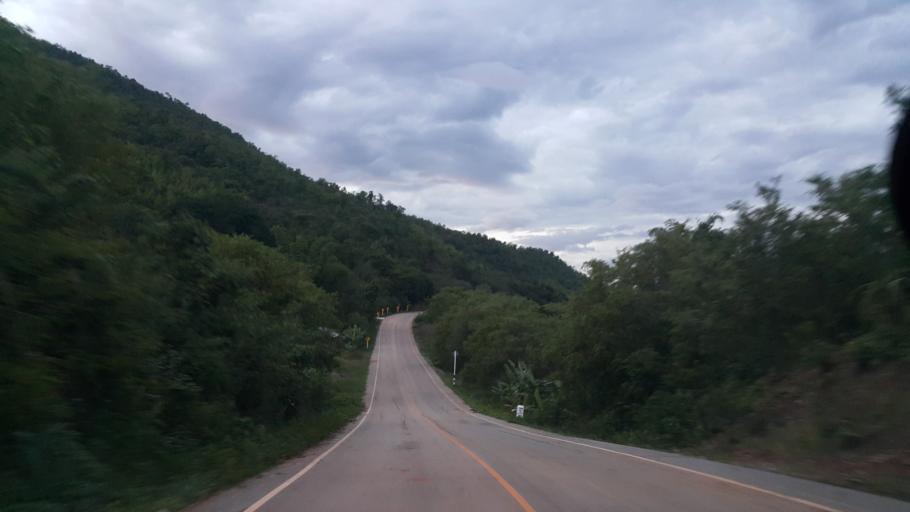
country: TH
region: Loei
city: Phu Ruea
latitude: 17.5097
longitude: 101.2336
